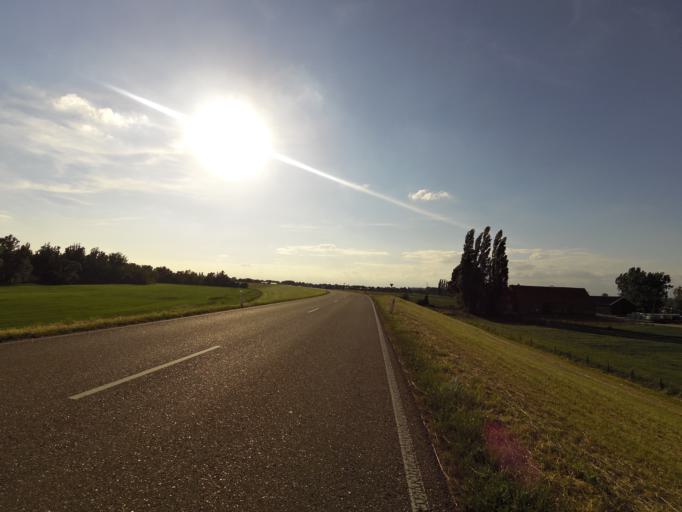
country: NL
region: Gelderland
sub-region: Gemeente Zevenaar
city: Zevenaar
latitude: 51.8842
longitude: 6.0622
